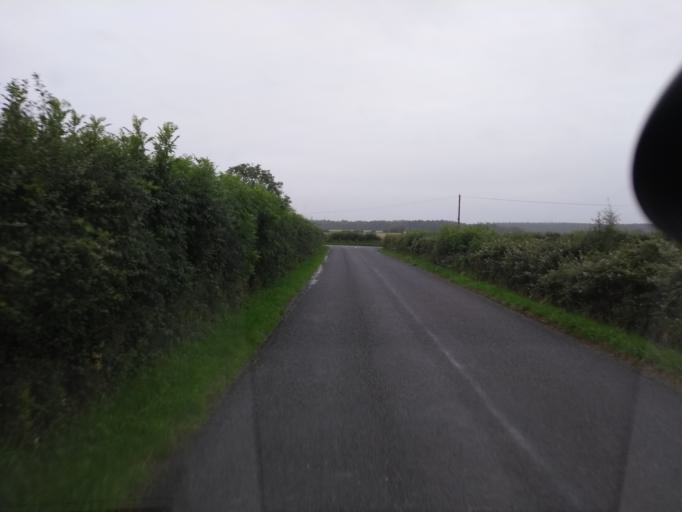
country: GB
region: England
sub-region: Somerset
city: Street
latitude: 51.0776
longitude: -2.6866
